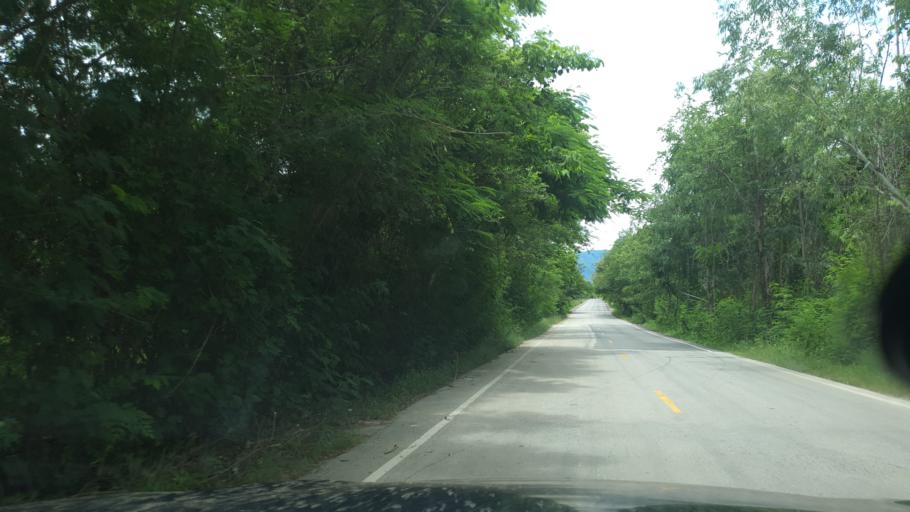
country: TH
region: Lampang
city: Sop Prap
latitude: 17.9256
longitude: 99.3795
